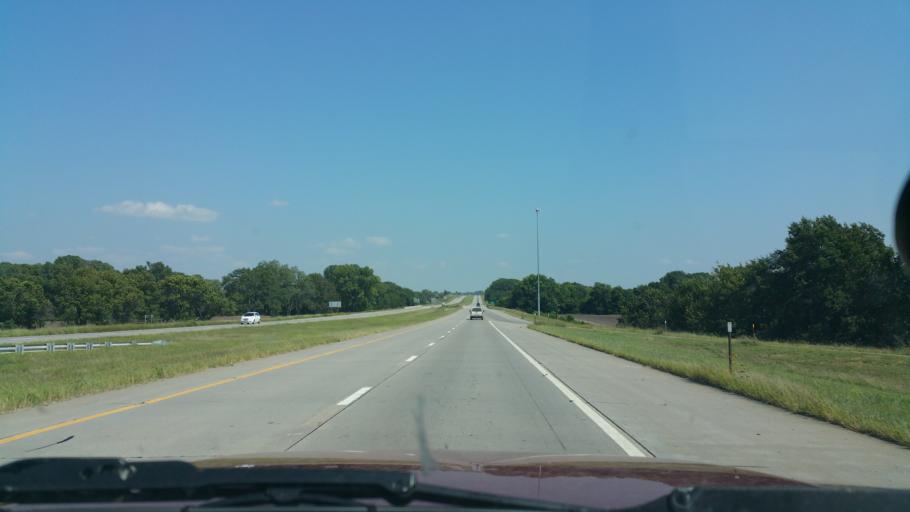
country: US
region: Kansas
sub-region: Dickinson County
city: Chapman
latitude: 38.9898
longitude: -97.0237
